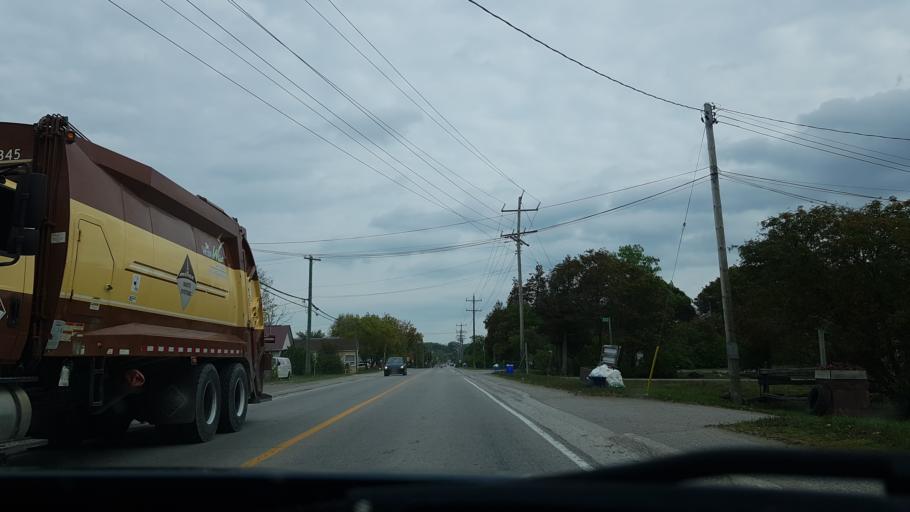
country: CA
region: Ontario
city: Omemee
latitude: 44.5329
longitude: -78.7464
